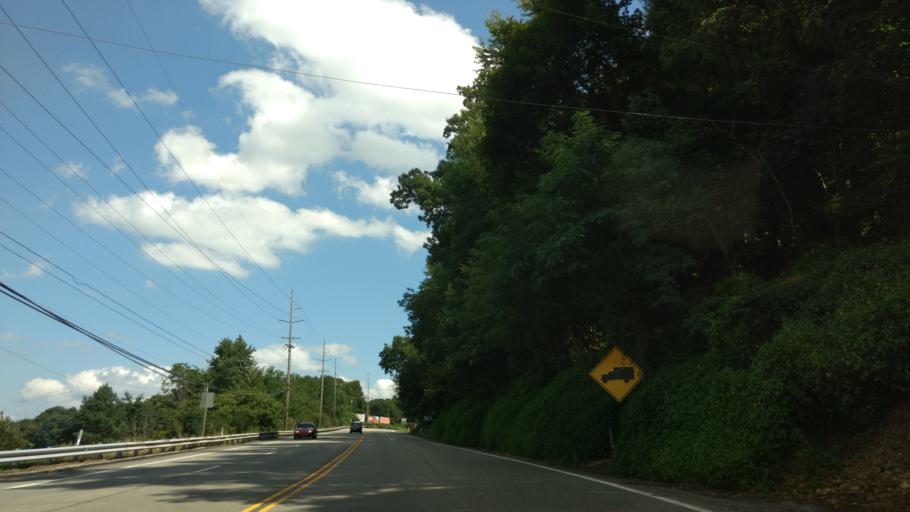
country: US
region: Pennsylvania
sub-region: Allegheny County
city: Franklin Park
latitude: 40.5846
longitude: -80.0425
